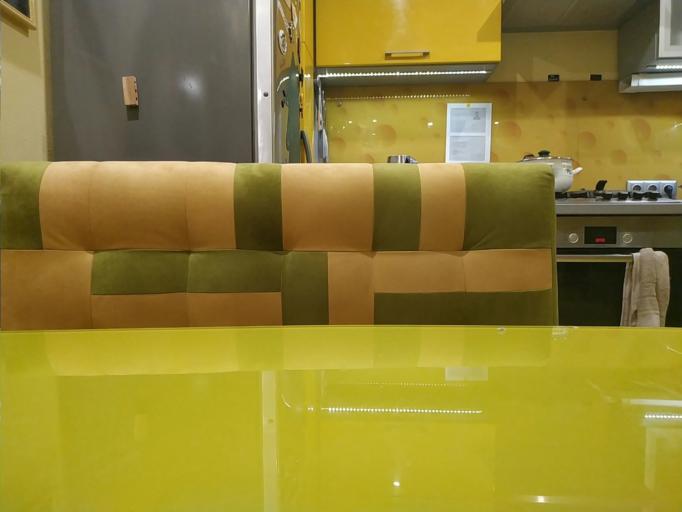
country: RU
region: Murmansk
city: Alakurtti
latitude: 66.1440
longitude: 30.3158
